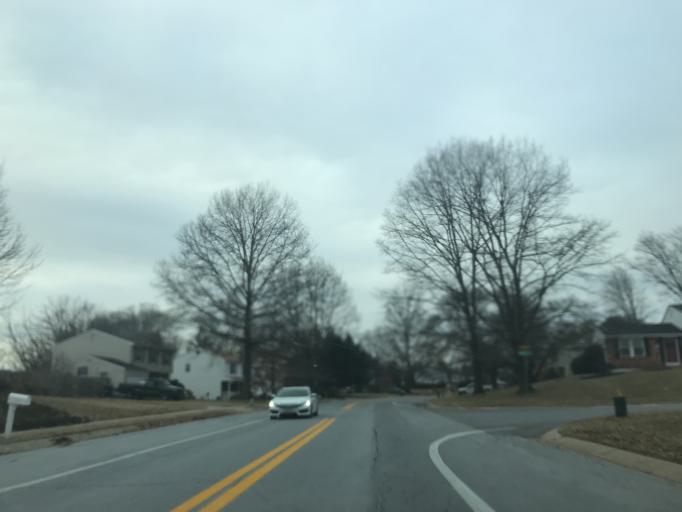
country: US
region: Maryland
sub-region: Carroll County
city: Eldersburg
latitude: 39.3867
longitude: -76.9327
